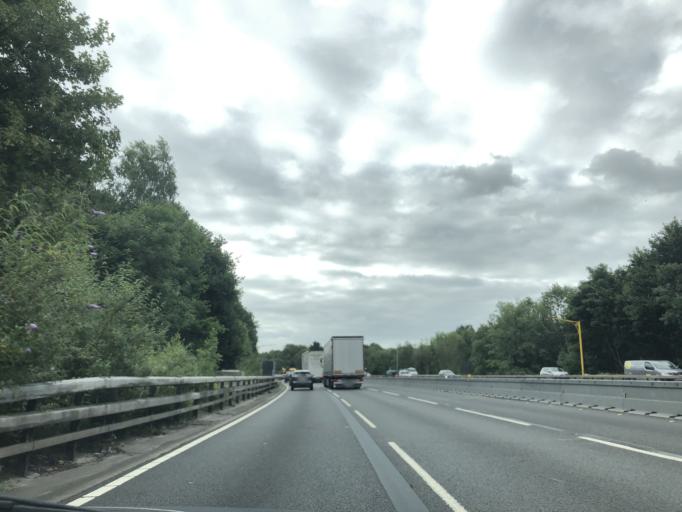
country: GB
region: England
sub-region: Hampshire
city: Bursledon
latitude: 50.8824
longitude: -1.2846
